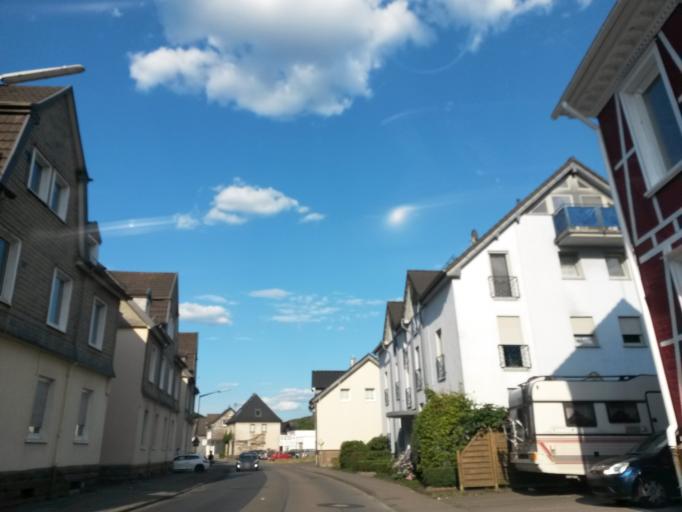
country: DE
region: North Rhine-Westphalia
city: Wiehl
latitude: 50.9818
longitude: 7.5207
